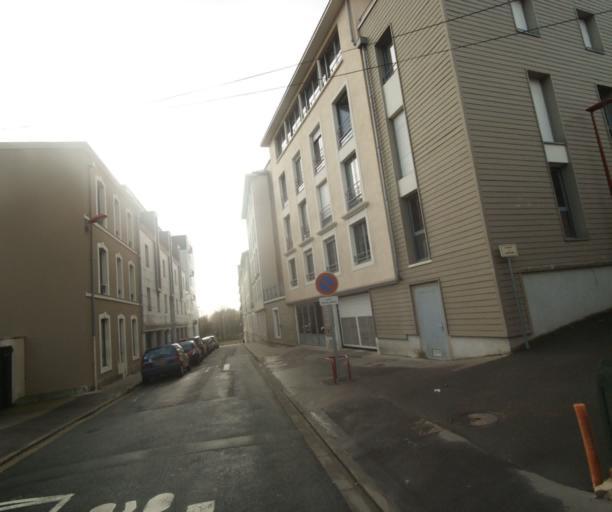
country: FR
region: Pays de la Loire
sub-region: Departement de la Sarthe
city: Le Mans
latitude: 48.0117
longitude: 0.2027
